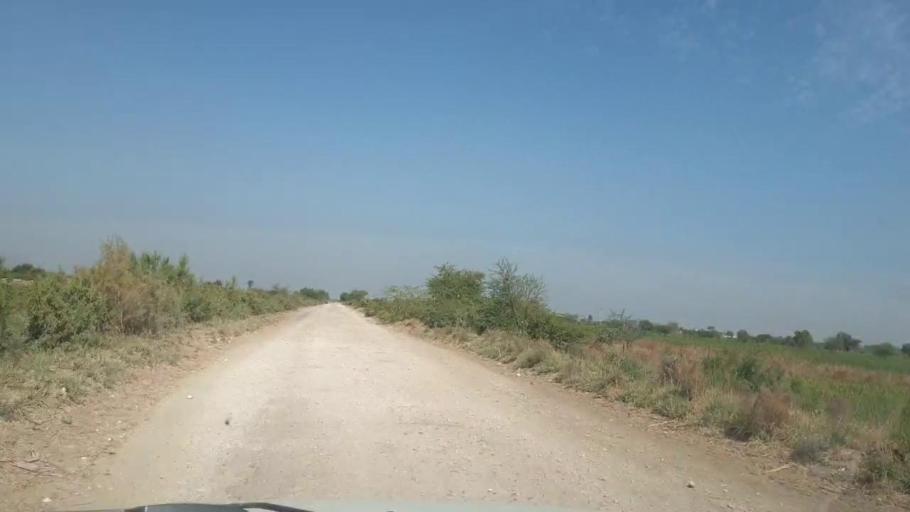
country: PK
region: Sindh
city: Mirpur Khas
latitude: 25.5925
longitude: 69.2010
